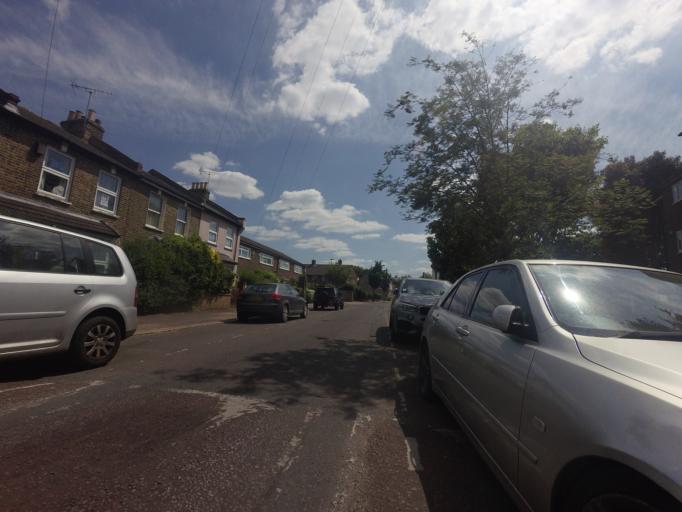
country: GB
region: England
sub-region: Greater London
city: East Ham
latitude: 51.5528
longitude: 0.0173
